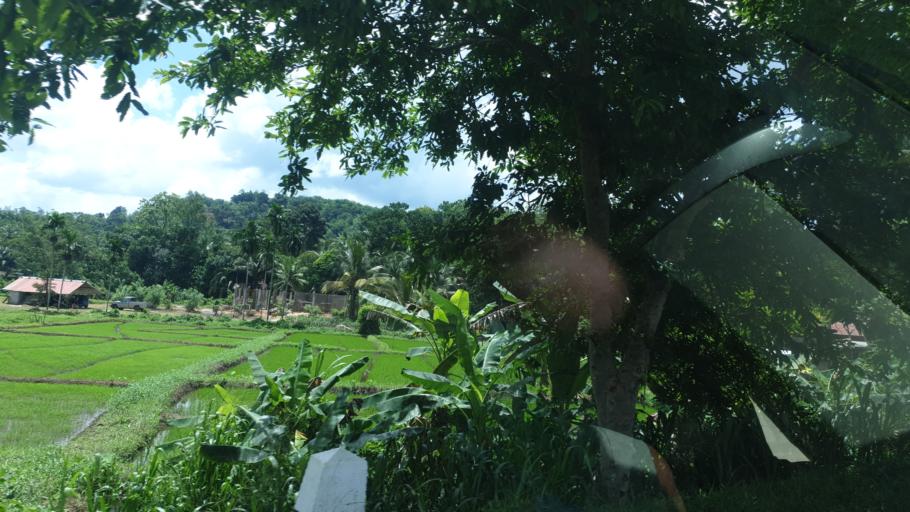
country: LK
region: Western
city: Horawala Junction
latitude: 6.5243
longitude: 80.2149
